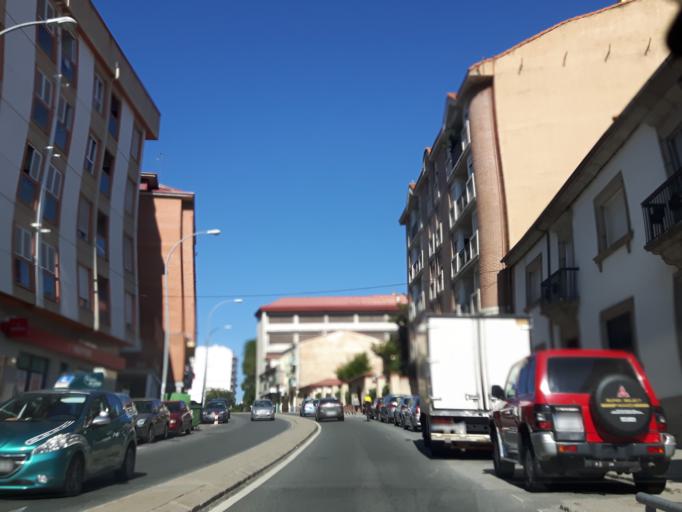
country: ES
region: Castille and Leon
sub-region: Provincia de Salamanca
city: Bejar
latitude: 40.3844
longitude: -5.7589
